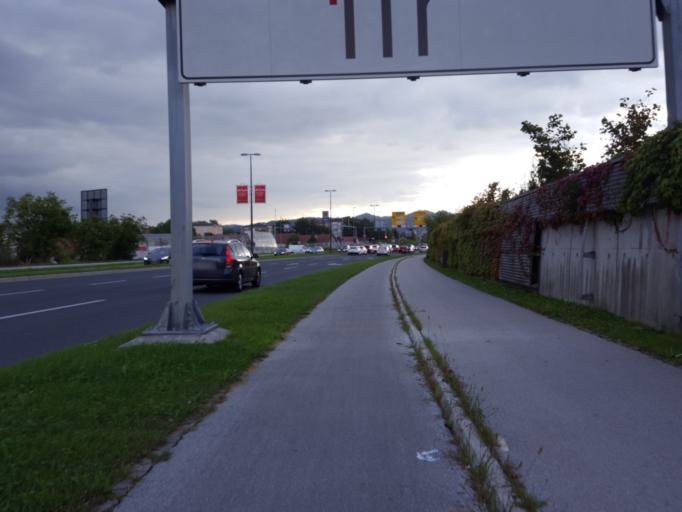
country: SI
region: Dol pri Ljubljani
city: Dol pri Ljubljani
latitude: 46.0550
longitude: 14.5710
